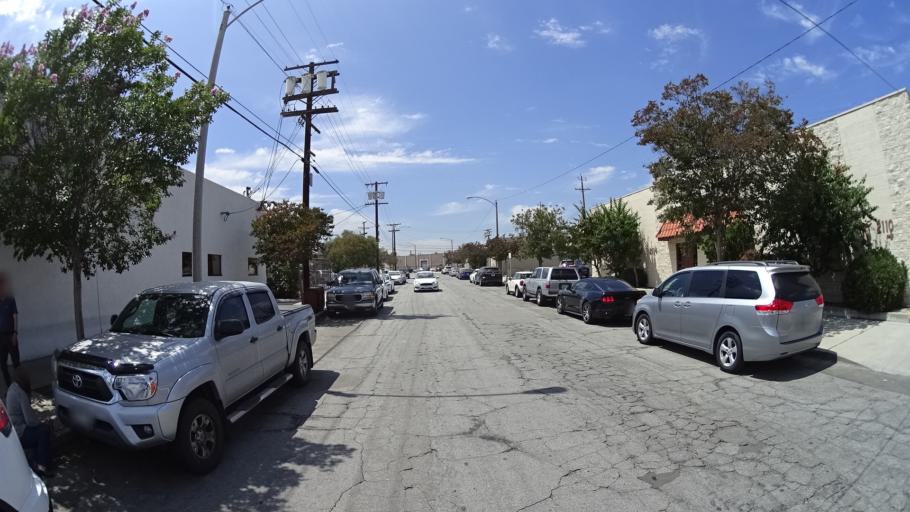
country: US
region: California
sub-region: Los Angeles County
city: Burbank
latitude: 34.1944
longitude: -118.3342
